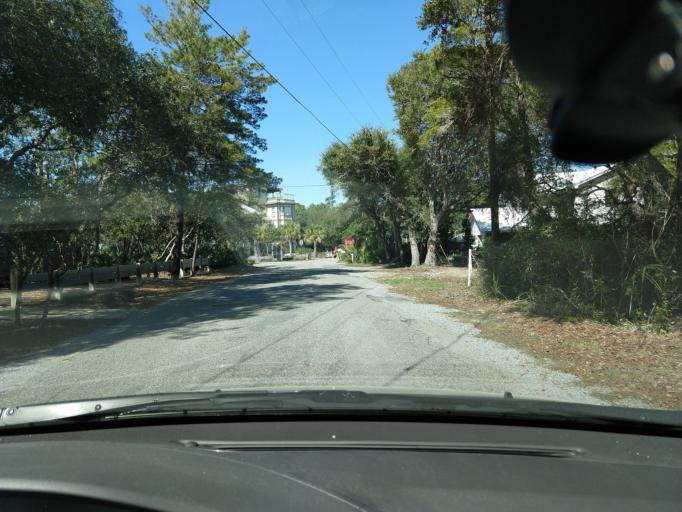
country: US
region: Florida
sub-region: Walton County
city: Seaside
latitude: 30.3388
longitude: -86.1971
